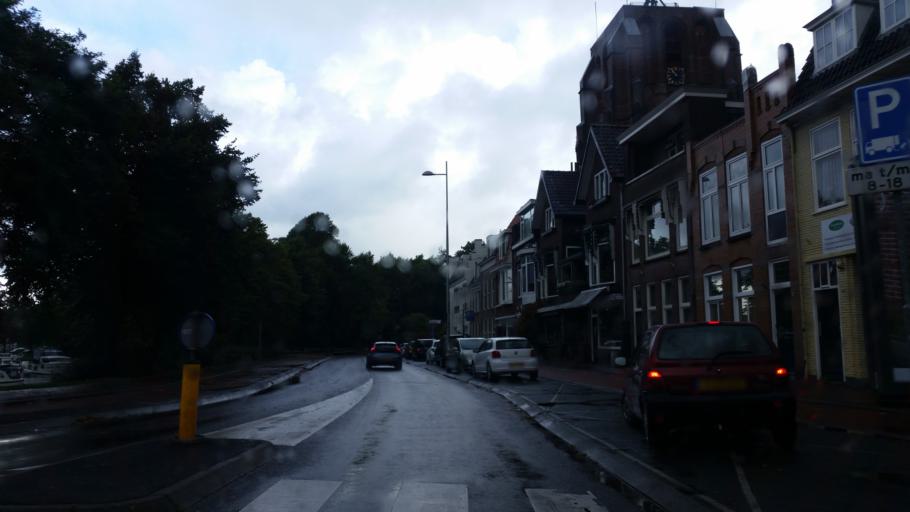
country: NL
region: Friesland
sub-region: Gemeente Leeuwarden
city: Bilgaard
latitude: 53.2023
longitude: 5.7891
